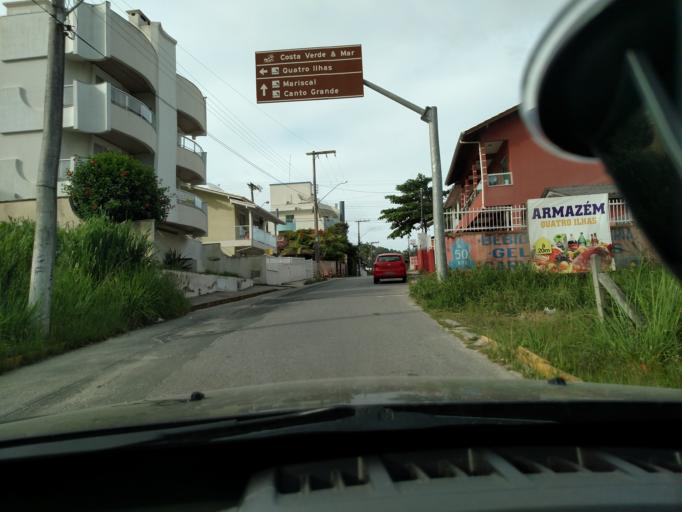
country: BR
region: Santa Catarina
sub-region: Porto Belo
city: Porto Belo
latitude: -27.1510
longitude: -48.4860
